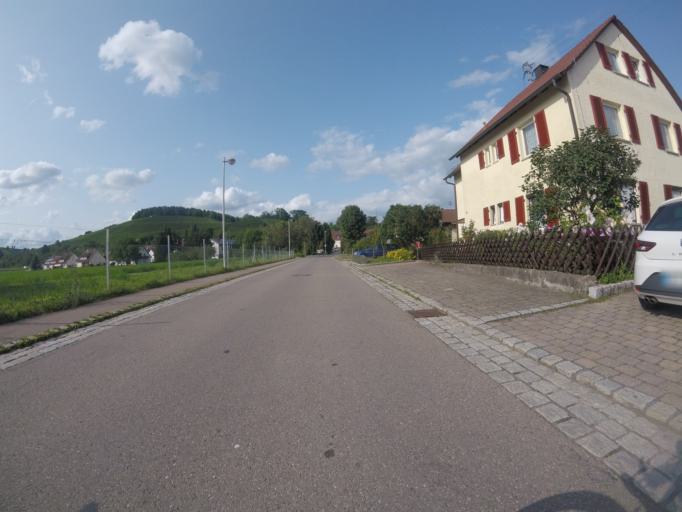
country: DE
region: Baden-Wuerttemberg
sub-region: Regierungsbezirk Stuttgart
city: Aspach
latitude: 48.9935
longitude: 9.3932
